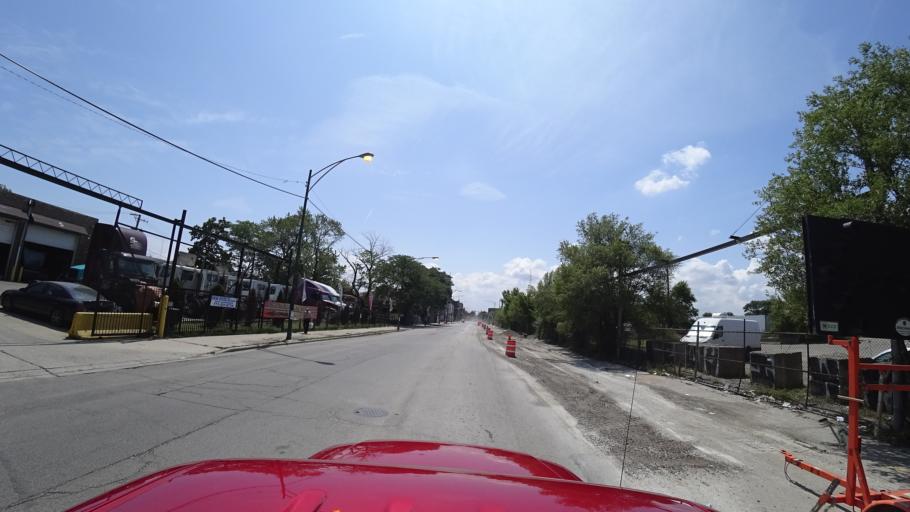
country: US
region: Illinois
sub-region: Cook County
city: Chicago
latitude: 41.8262
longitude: -87.6947
